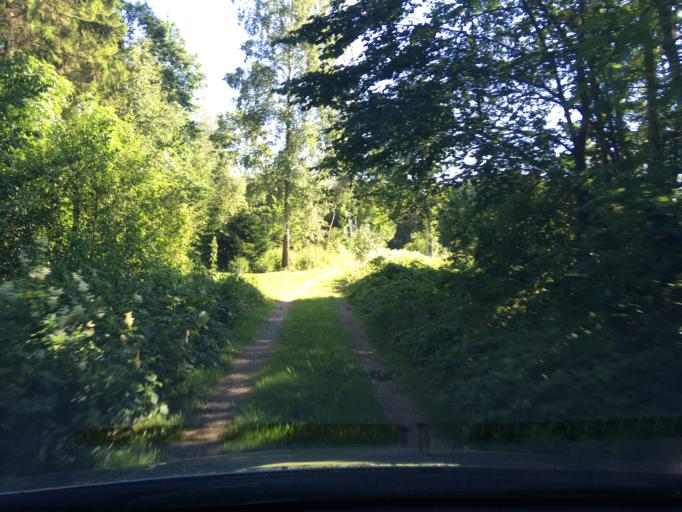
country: EE
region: Laeaene
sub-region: Lihula vald
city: Lihula
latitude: 58.5878
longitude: 23.7368
